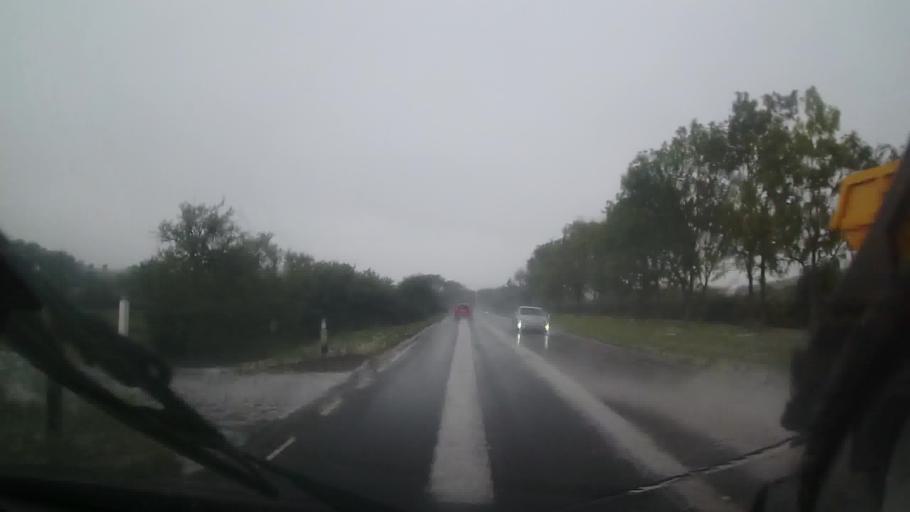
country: GB
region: England
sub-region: Worcestershire
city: Evesham
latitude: 52.1158
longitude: -1.9676
